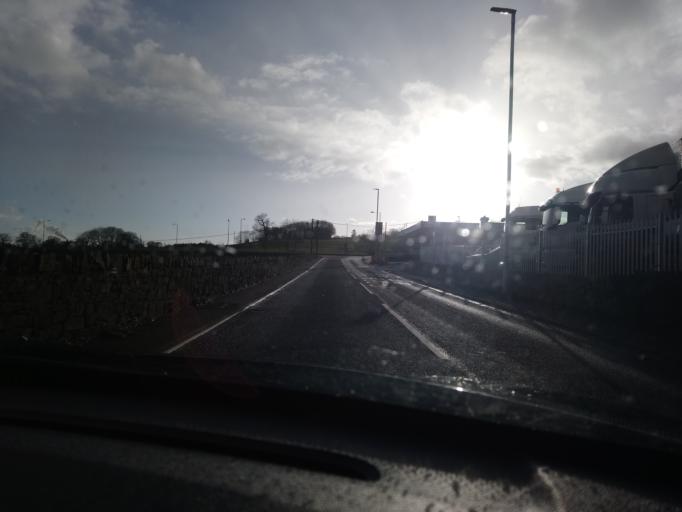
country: GB
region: Wales
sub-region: Wrexham
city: Chirk
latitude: 52.9574
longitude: -3.0666
